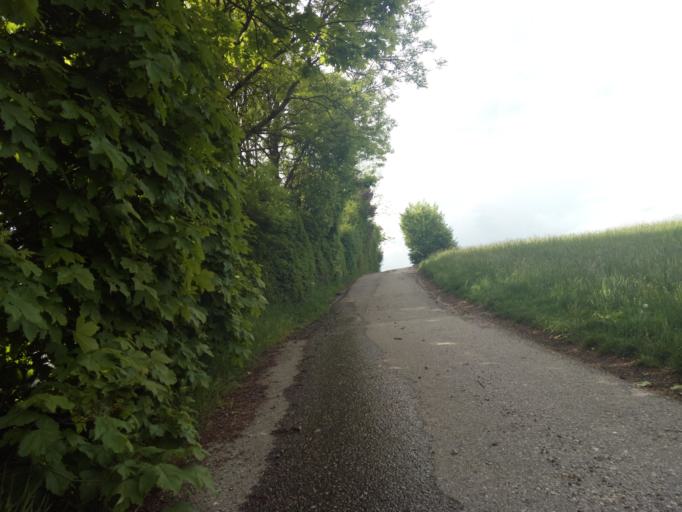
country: AT
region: Lower Austria
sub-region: Politischer Bezirk Modling
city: Breitenfurt bei Wien
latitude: 48.1357
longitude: 16.1281
